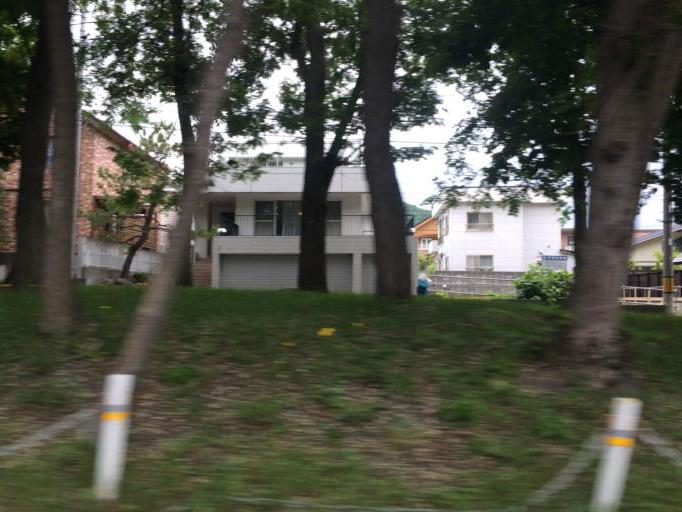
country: JP
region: Hokkaido
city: Sapporo
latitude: 43.0536
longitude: 141.3036
